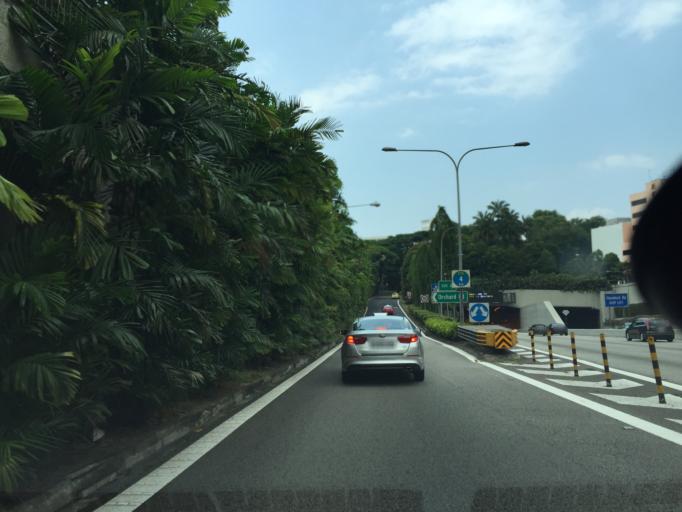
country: SG
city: Singapore
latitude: 1.3026
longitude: 103.8417
